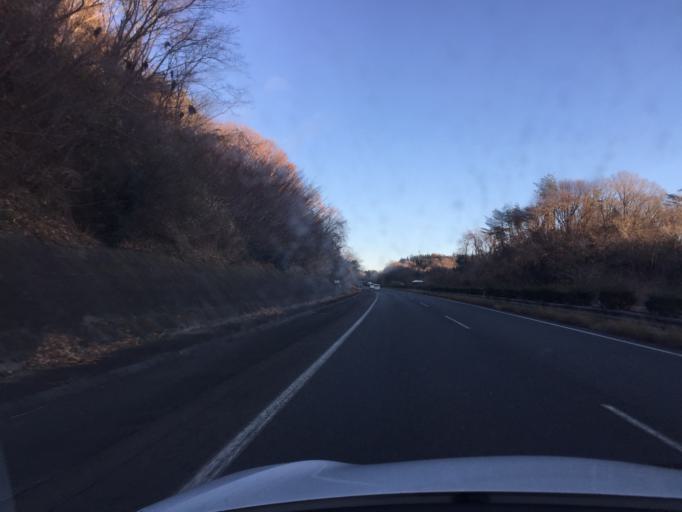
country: JP
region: Fukushima
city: Iwaki
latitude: 36.9544
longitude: 140.7791
